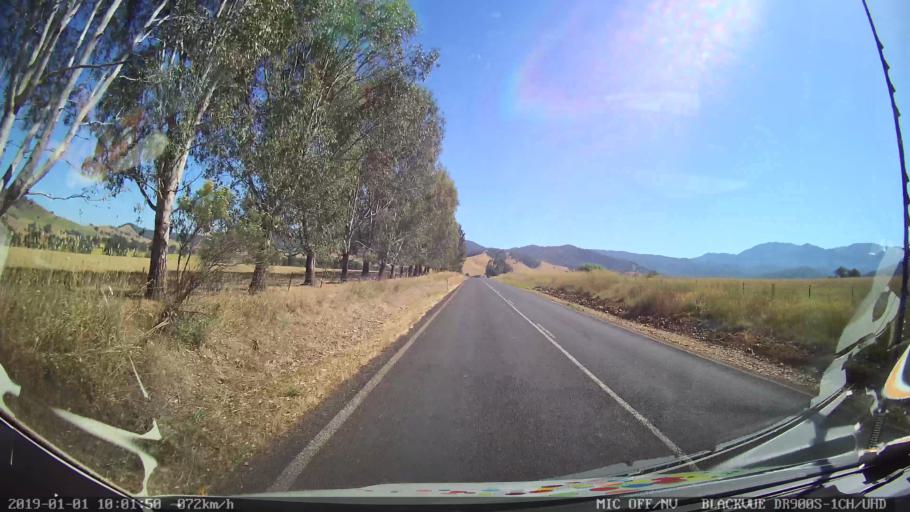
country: AU
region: New South Wales
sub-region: Snowy River
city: Jindabyne
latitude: -36.1874
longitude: 148.1009
